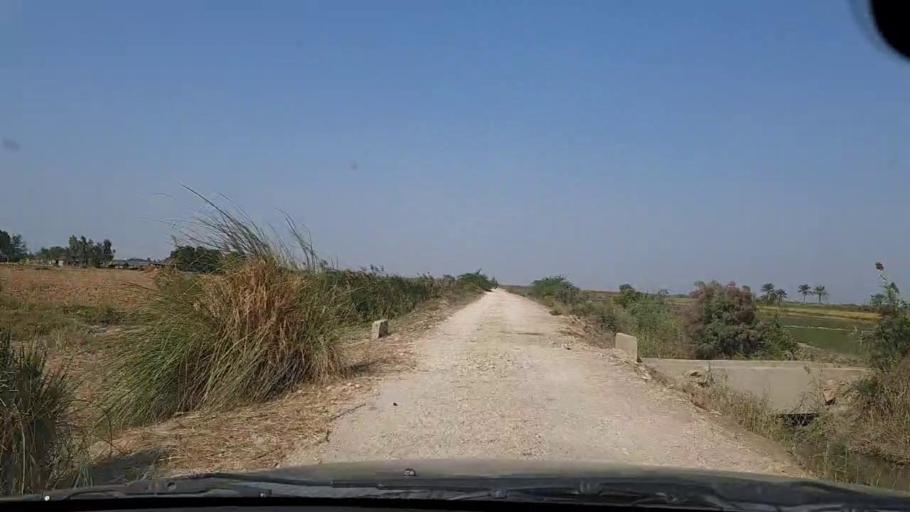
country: PK
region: Sindh
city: Mirpur Sakro
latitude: 24.3738
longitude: 67.6830
